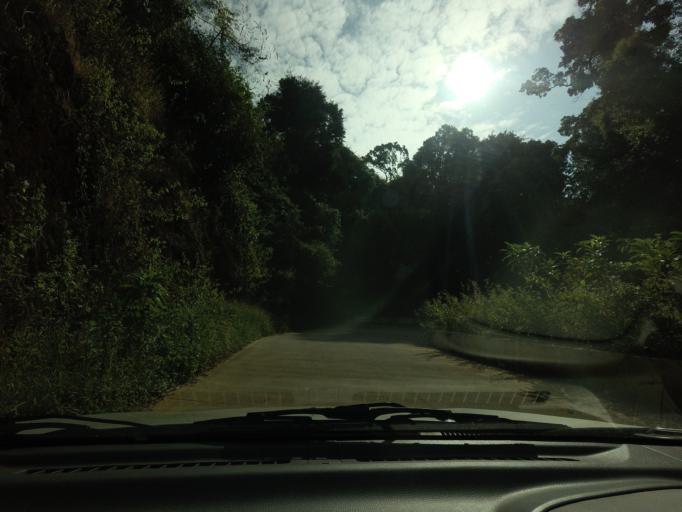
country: IN
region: Karnataka
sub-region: Kodagu
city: Sanivarsante
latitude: 12.7277
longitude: 75.6621
